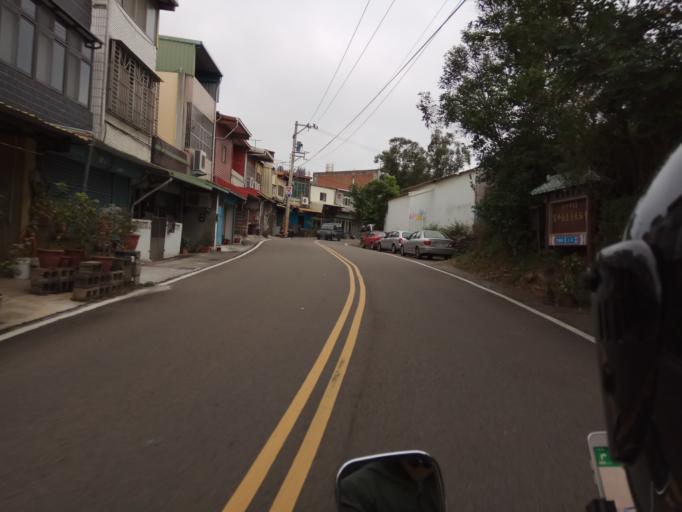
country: TW
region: Taiwan
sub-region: Hsinchu
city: Hsinchu
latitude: 24.7775
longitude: 120.9782
